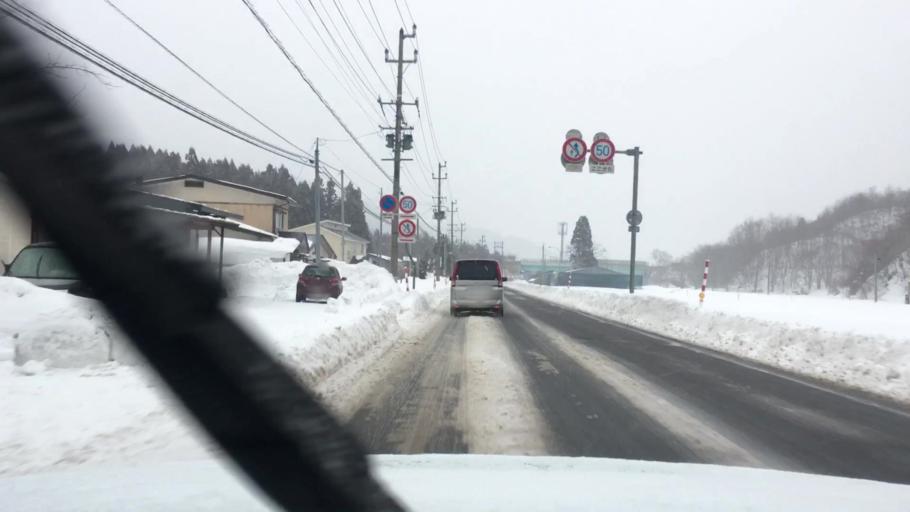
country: JP
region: Akita
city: Hanawa
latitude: 40.0438
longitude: 140.9989
